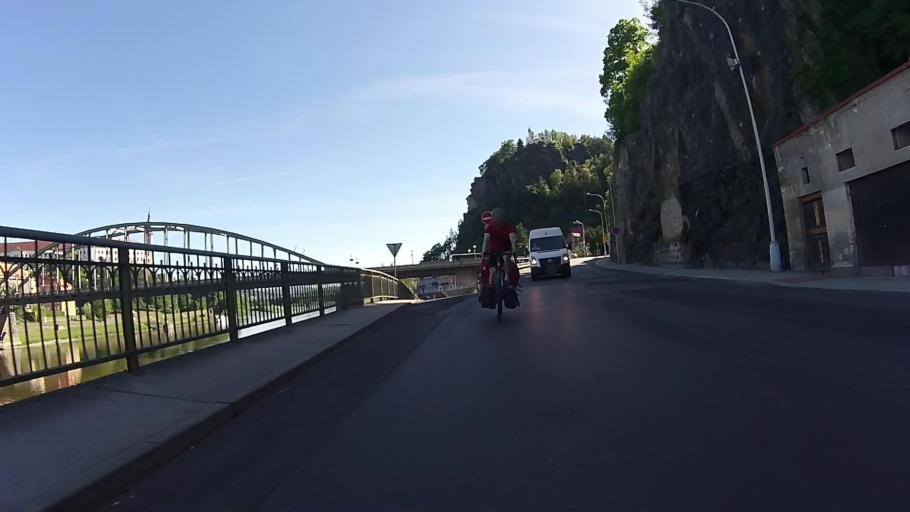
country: CZ
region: Ustecky
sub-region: Okres Decin
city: Decin
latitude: 50.7822
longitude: 14.2072
